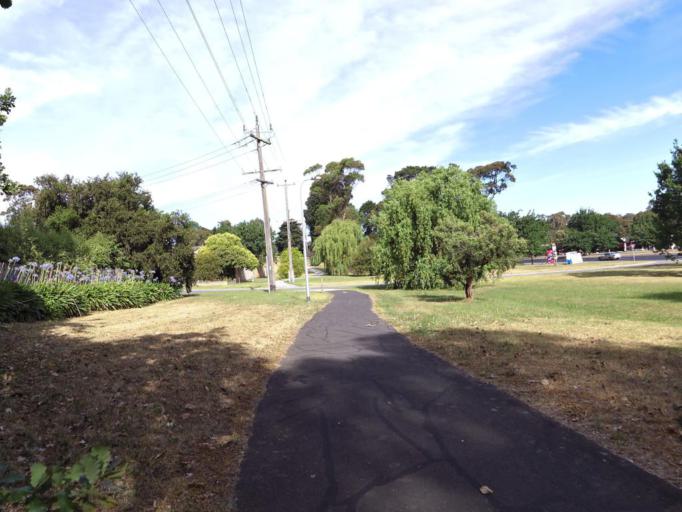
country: AU
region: Victoria
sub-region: Casey
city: Berwick
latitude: -38.0302
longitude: 145.3392
